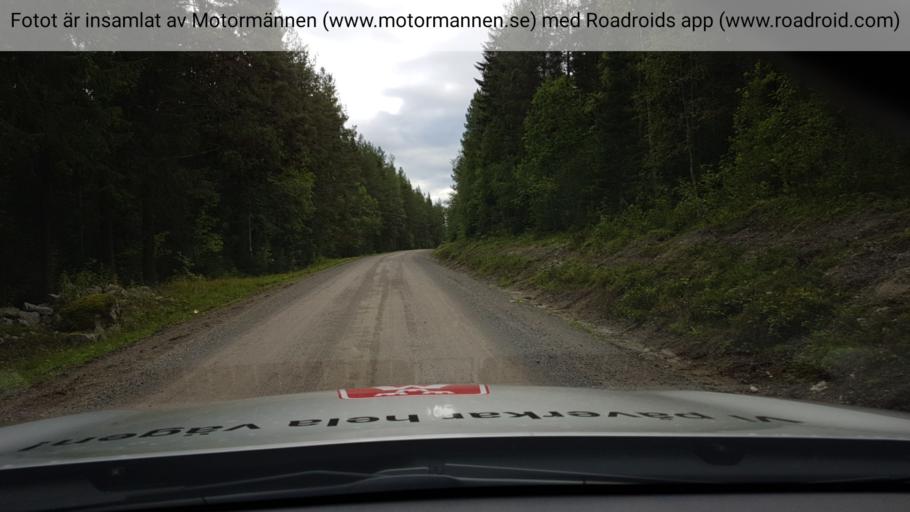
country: SE
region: Jaemtland
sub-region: Ragunda Kommun
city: Hammarstrand
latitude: 62.9486
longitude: 16.1106
